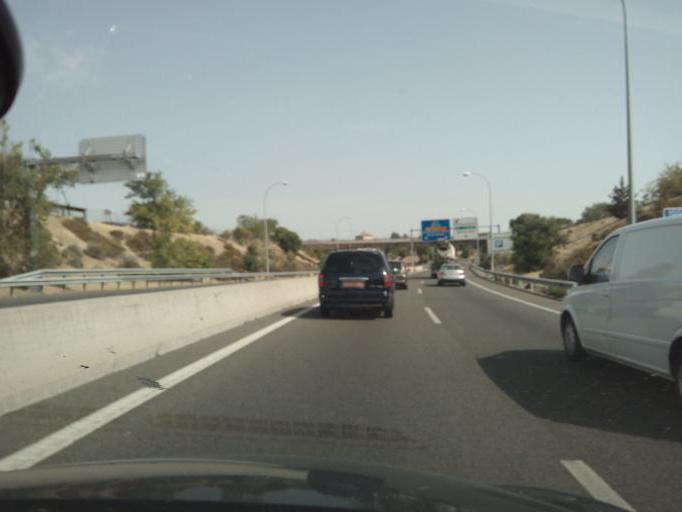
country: ES
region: Madrid
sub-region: Provincia de Madrid
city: Barajas de Madrid
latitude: 40.4644
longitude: -3.5807
